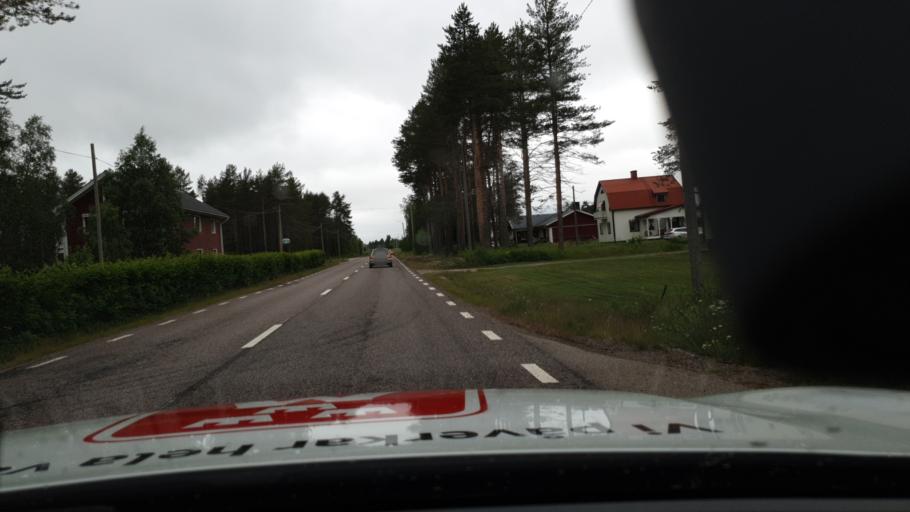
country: FI
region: Lapland
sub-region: Torniolaakso
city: Pello
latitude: 66.9783
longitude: 23.8023
